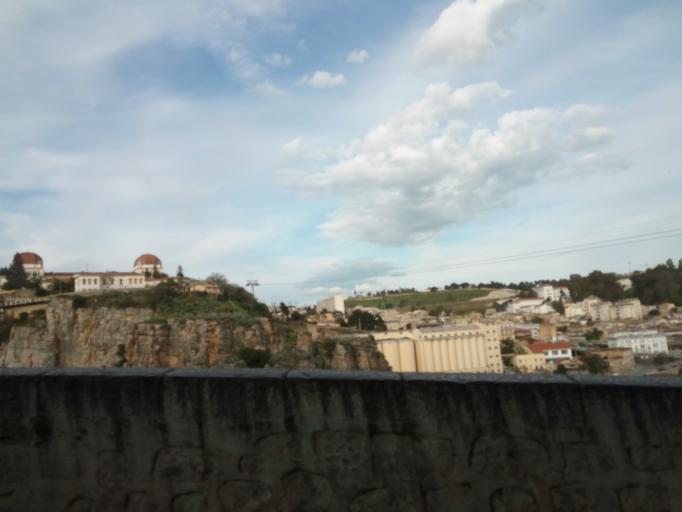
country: DZ
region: Constantine
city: Constantine
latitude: 36.3705
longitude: 6.6146
